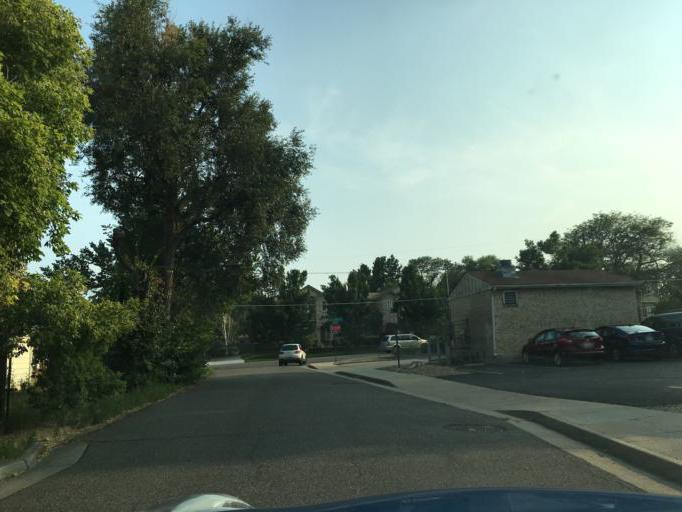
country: US
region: Colorado
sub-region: Arapahoe County
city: Glendale
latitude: 39.6935
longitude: -104.9340
